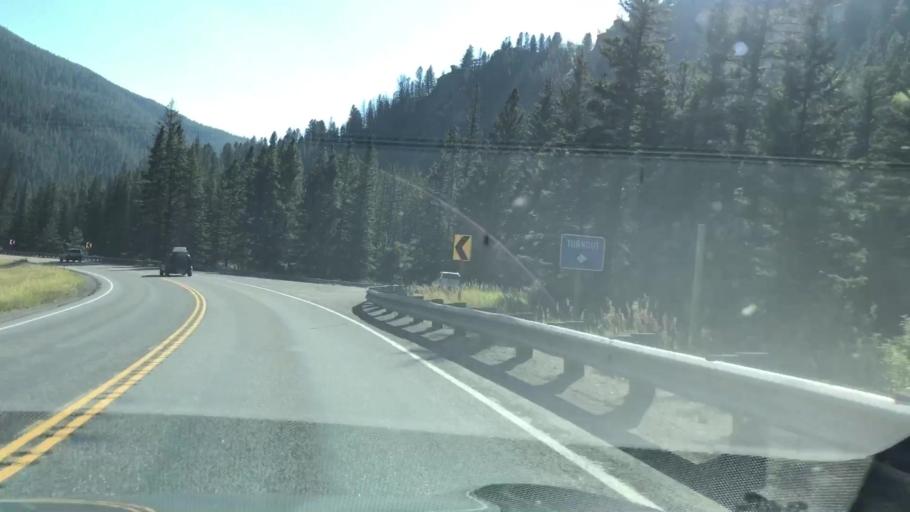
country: US
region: Montana
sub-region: Gallatin County
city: Big Sky
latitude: 45.3070
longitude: -111.1962
